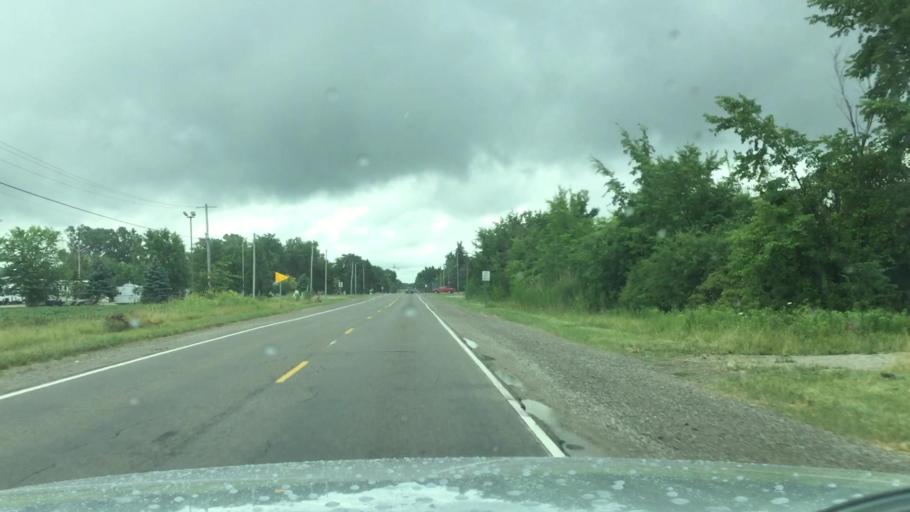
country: US
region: Michigan
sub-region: Genesee County
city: Flushing
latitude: 43.0699
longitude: -83.7732
